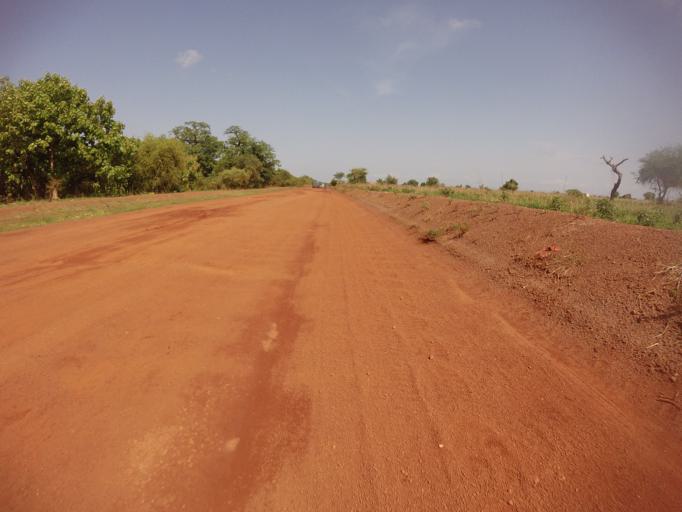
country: GH
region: Upper East
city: Bawku
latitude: 11.0032
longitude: -0.1977
